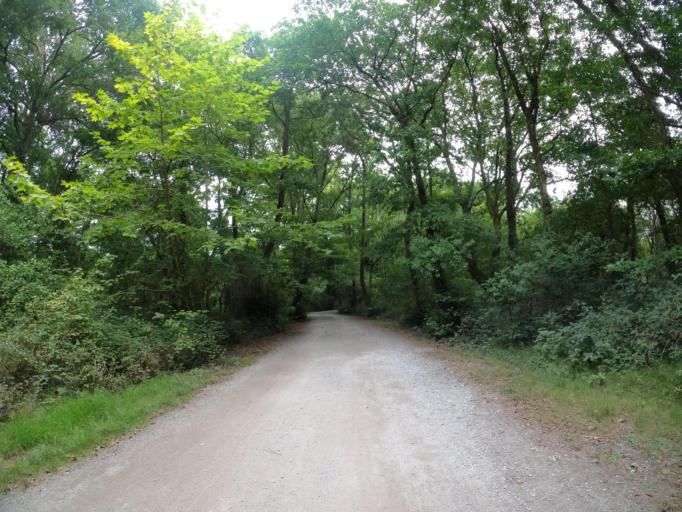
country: FR
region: Aquitaine
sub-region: Departement des Landes
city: Leon
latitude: 43.8866
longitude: -1.3084
